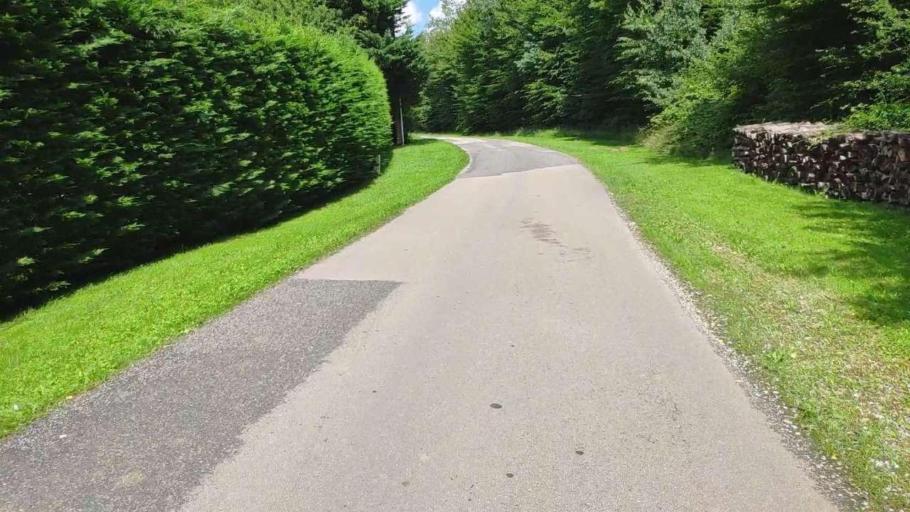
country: FR
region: Franche-Comte
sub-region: Departement du Jura
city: Chaussin
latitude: 46.8857
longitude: 5.4647
